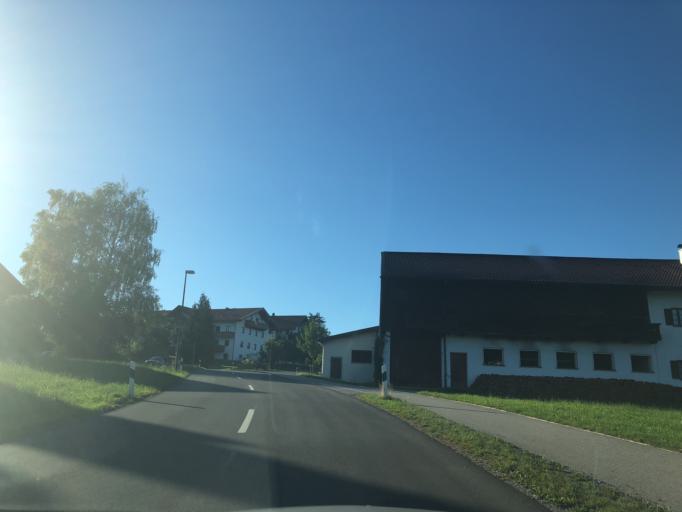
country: DE
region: Bavaria
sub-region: Upper Bavaria
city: Prien am Chiemsee
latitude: 47.8566
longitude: 12.3325
